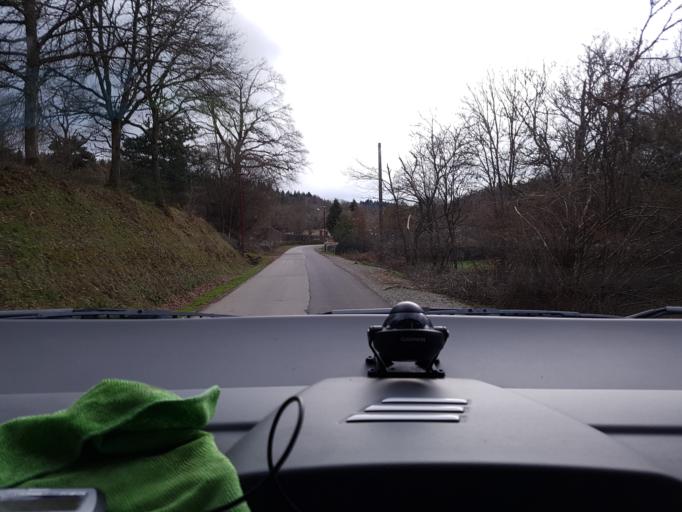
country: FR
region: Auvergne
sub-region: Departement du Puy-de-Dome
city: Saint-Ours
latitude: 45.8456
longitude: 2.8564
